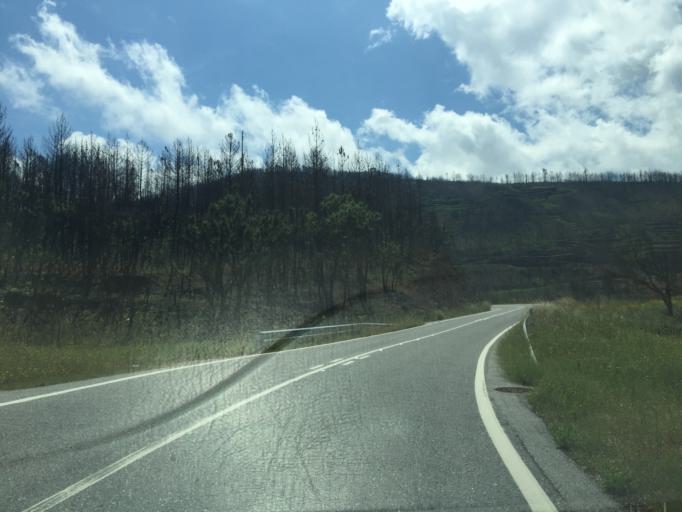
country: PT
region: Coimbra
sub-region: Pampilhosa da Serra
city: Pampilhosa da Serra
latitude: 39.9809
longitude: -7.9578
